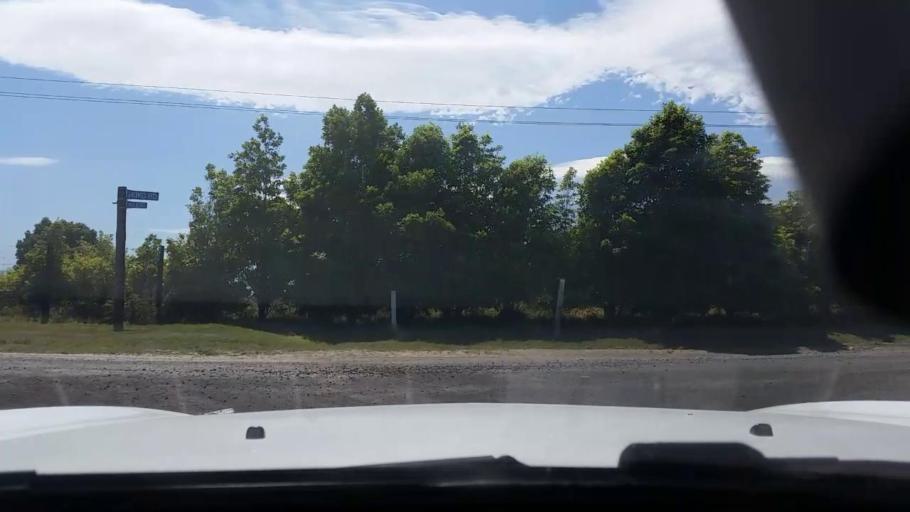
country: NZ
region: Bay of Plenty
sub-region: Rotorua District
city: Rotorua
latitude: -38.0232
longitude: 176.2754
